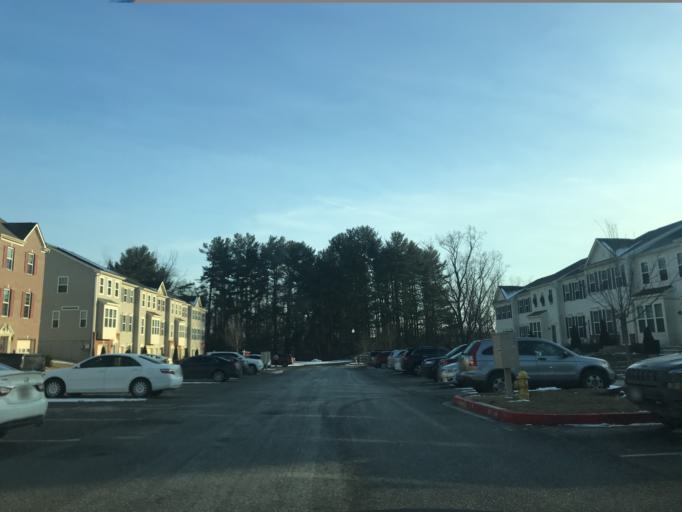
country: US
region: Maryland
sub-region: Harford County
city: Edgewood
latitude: 39.4063
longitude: -76.3318
